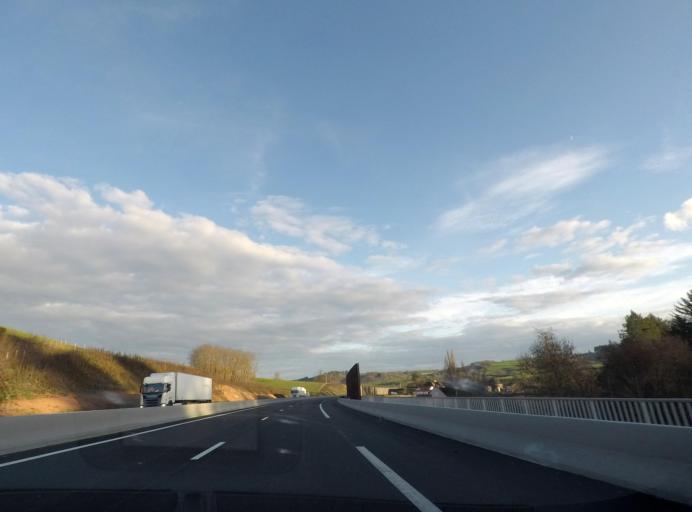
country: FR
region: Bourgogne
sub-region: Departement de Saone-et-Loire
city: Matour
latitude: 46.3813
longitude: 4.4856
